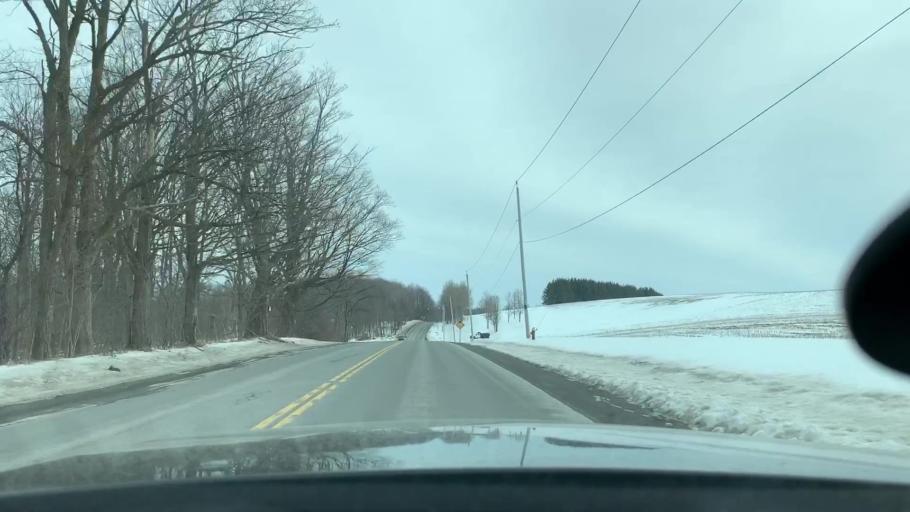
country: US
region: New York
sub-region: Oneida County
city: Washington Mills
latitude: 43.0453
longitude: -75.2211
